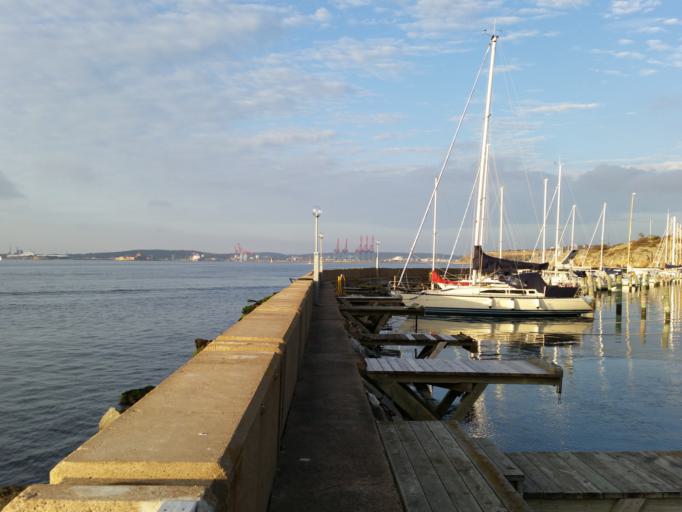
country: SE
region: Vaestra Goetaland
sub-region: Goteborg
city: Styrso
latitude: 57.6611
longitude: 11.8366
